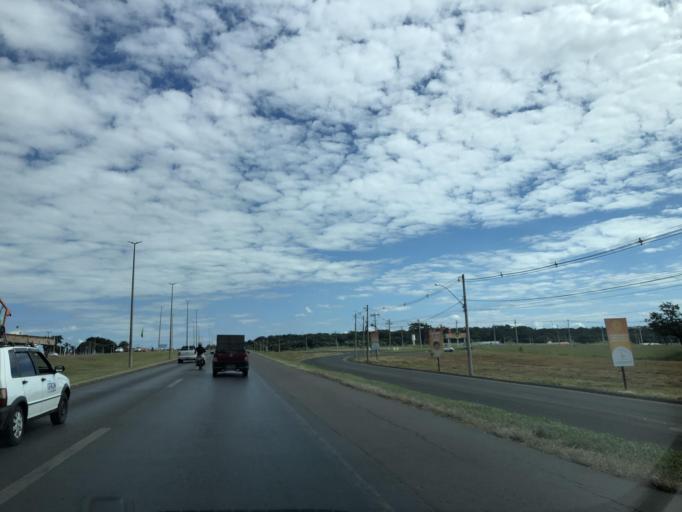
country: BR
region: Goias
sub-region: Luziania
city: Luziania
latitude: -16.0992
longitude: -47.9781
